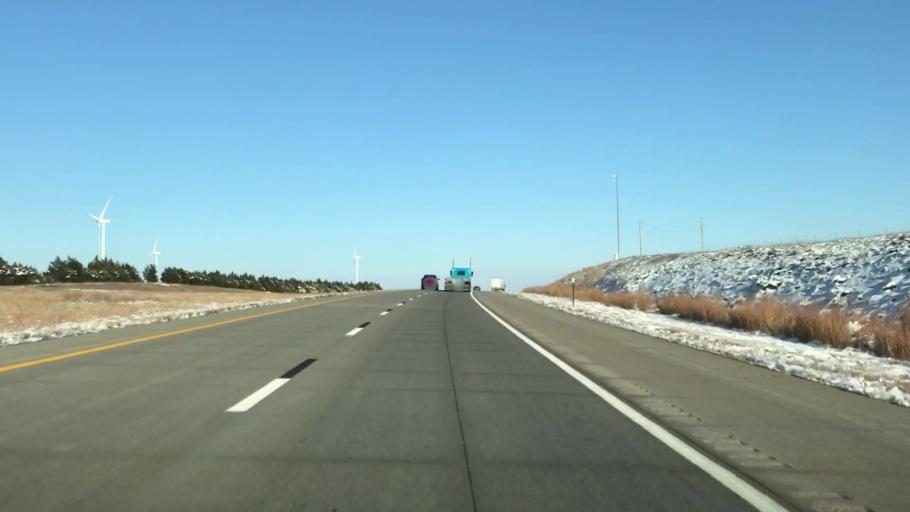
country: US
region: Kansas
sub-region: Lincoln County
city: Lincoln
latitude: 38.8736
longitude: -98.0542
